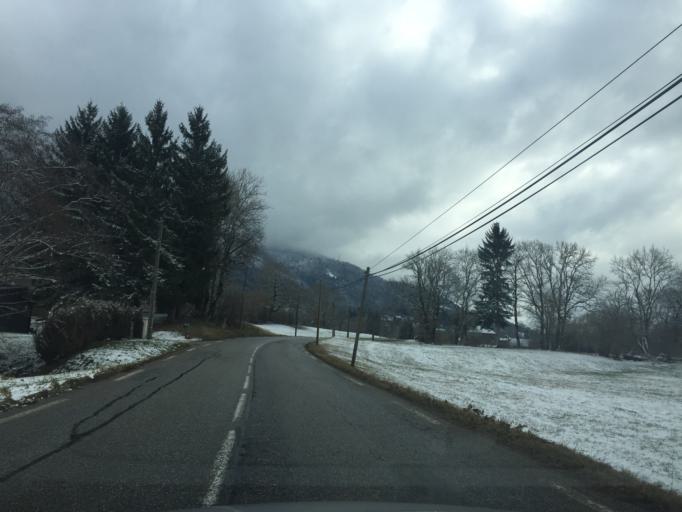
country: FR
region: Rhone-Alpes
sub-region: Departement de la Haute-Savoie
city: Gruffy
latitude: 45.7055
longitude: 6.1184
